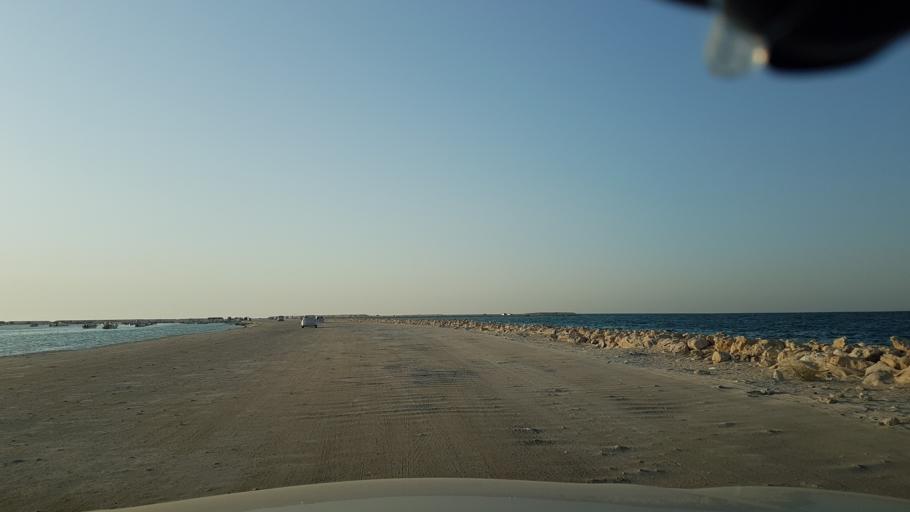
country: BH
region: Manama
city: Jidd Hafs
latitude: 26.2513
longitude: 50.5021
